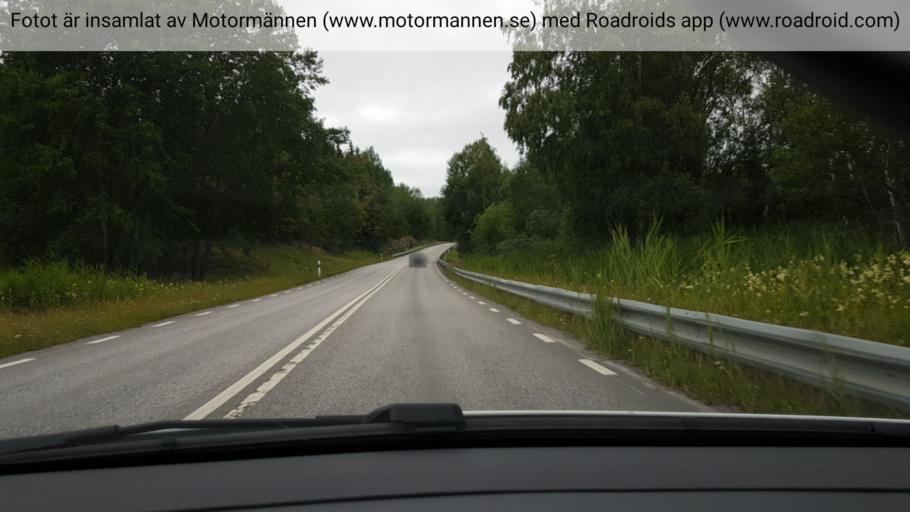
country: SE
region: Stockholm
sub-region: Osterakers Kommun
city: Akersberga
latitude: 59.4270
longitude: 18.2538
